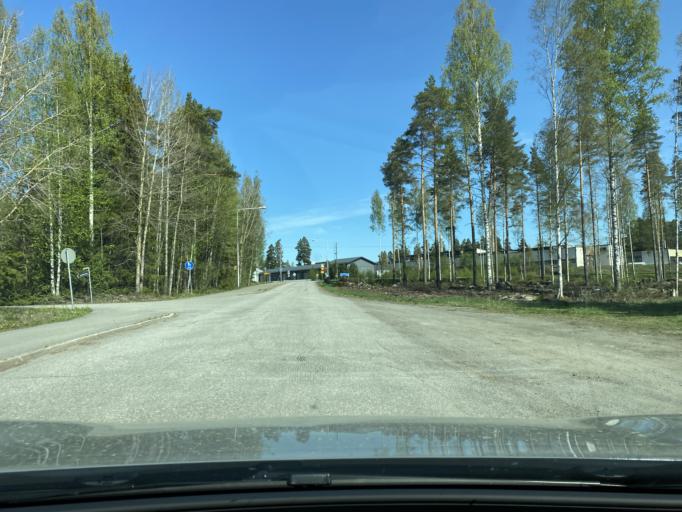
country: FI
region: Pirkanmaa
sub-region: Lounais-Pirkanmaa
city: Vammala
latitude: 61.3531
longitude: 22.8810
